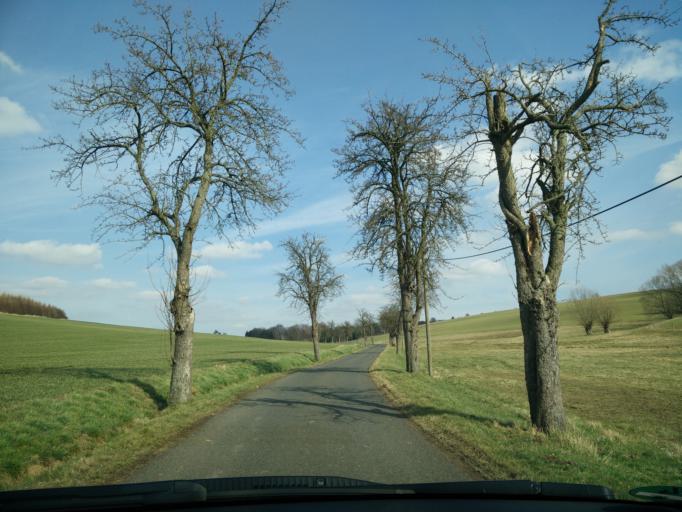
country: DE
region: Saxony
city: Zettlitz
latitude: 51.0860
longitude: 12.8128
